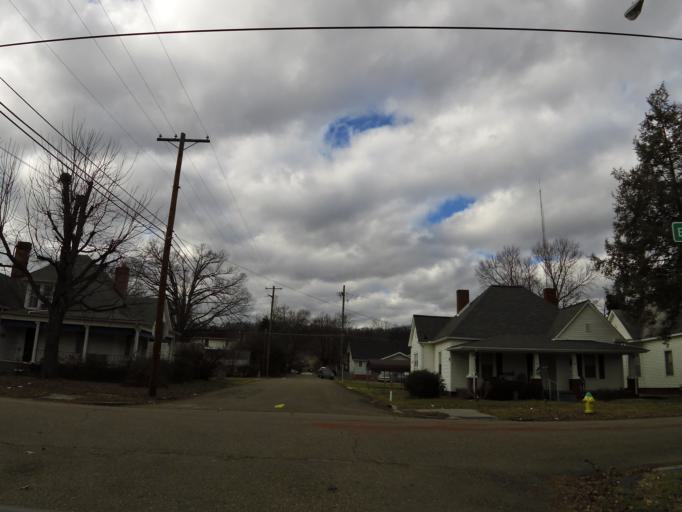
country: US
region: Tennessee
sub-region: Knox County
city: Knoxville
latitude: 35.9919
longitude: -83.9378
